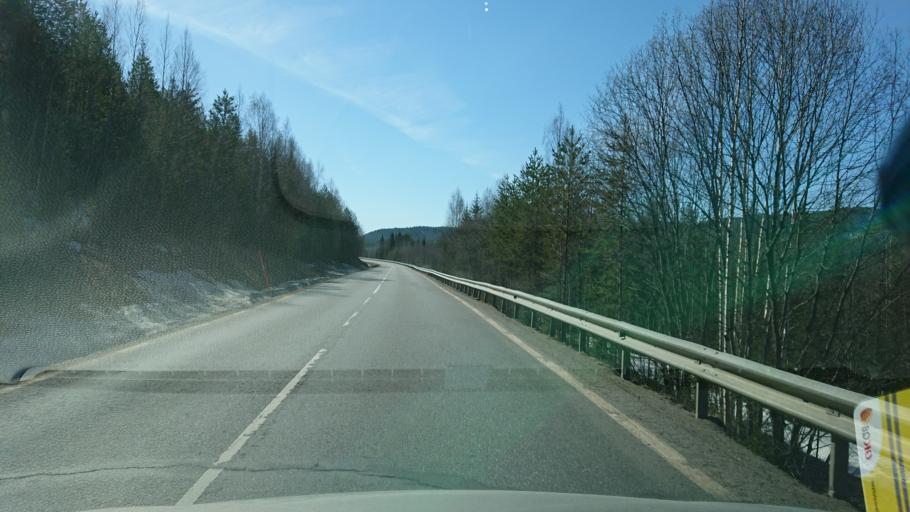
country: SE
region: Vaesterbotten
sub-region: Dorotea Kommun
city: Dorotea
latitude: 64.0446
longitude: 16.2583
